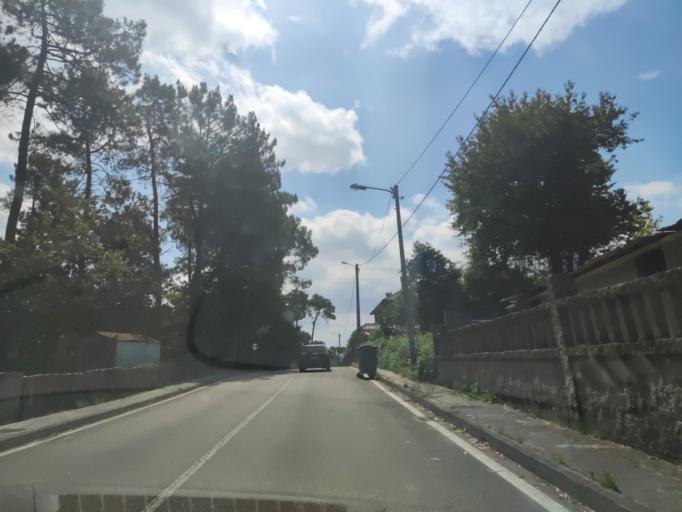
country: ES
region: Galicia
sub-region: Provincia de Pontevedra
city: Porrino
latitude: 42.1488
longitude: -8.6492
